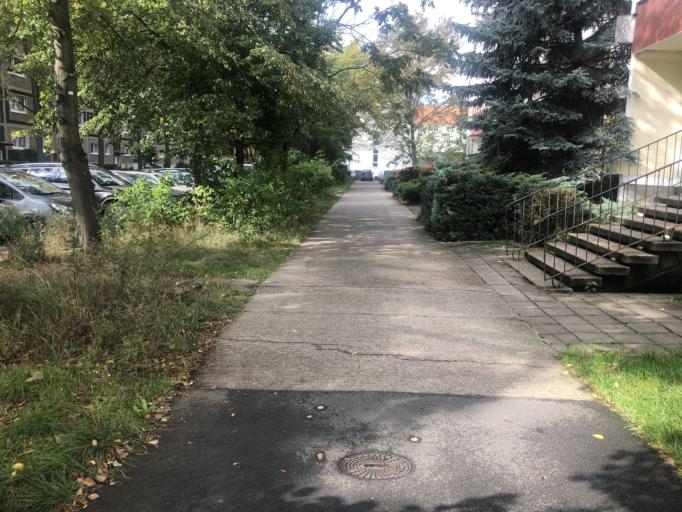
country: DE
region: Saxony-Anhalt
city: Dessau
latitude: 51.8158
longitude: 12.2442
